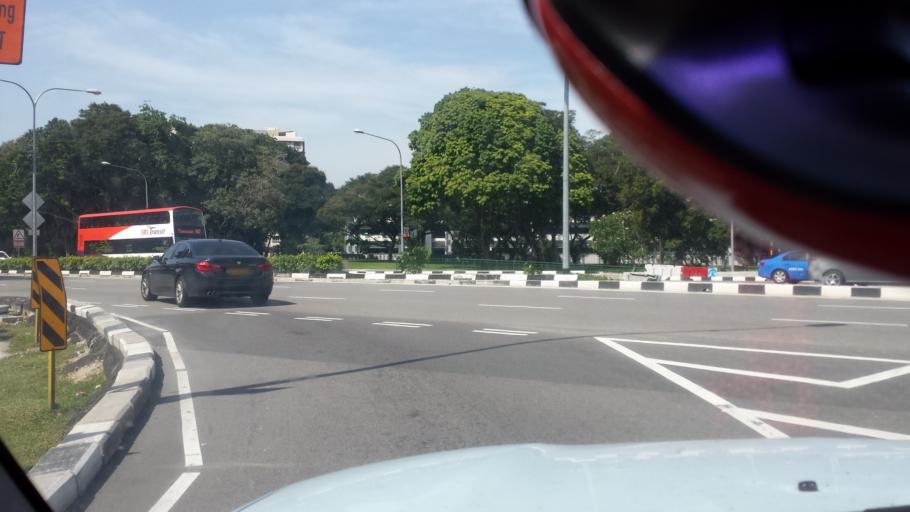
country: SG
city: Singapore
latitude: 1.3086
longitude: 103.8771
